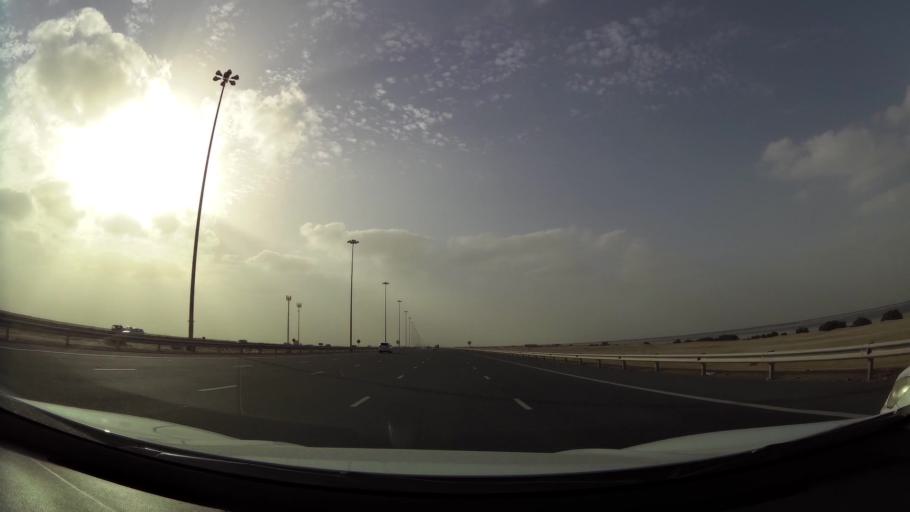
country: AE
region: Abu Dhabi
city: Abu Dhabi
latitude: 24.5151
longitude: 54.5397
